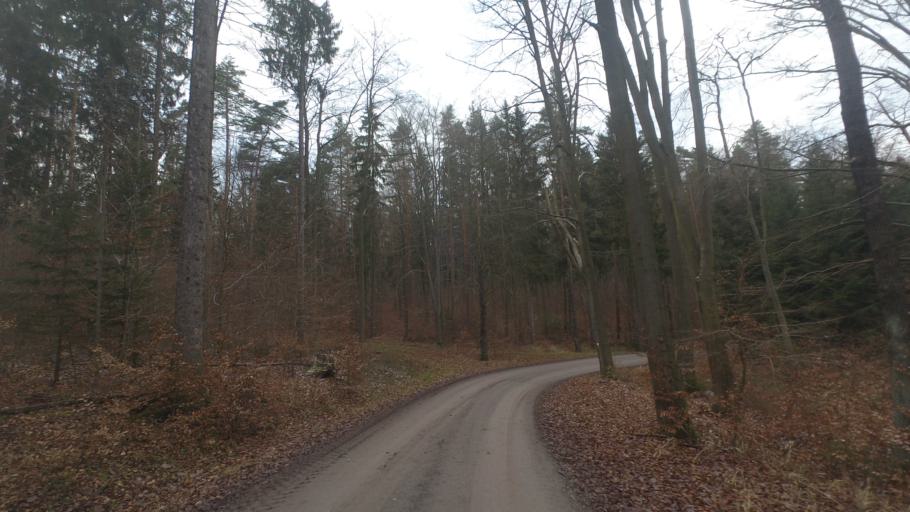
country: DE
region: Thuringia
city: Konitz
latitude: 50.6980
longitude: 11.4645
